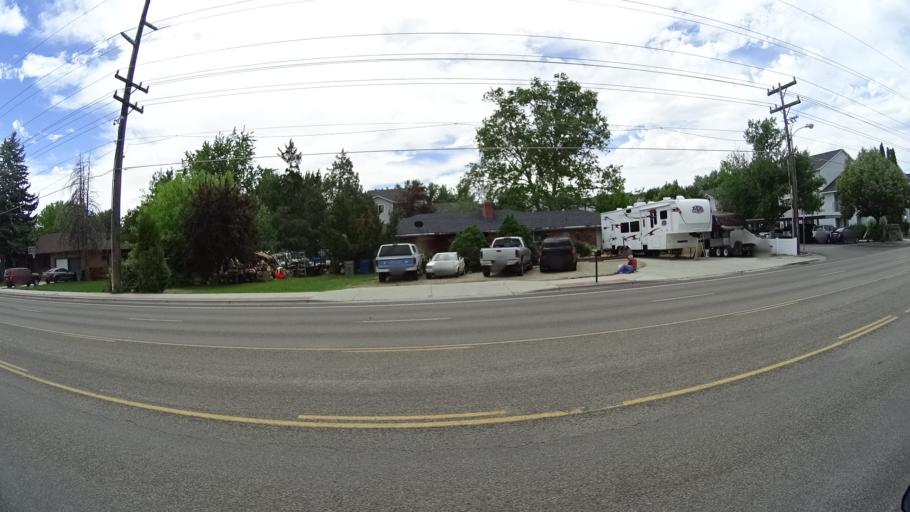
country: US
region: Idaho
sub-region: Ada County
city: Garden City
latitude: 43.6341
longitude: -116.2796
